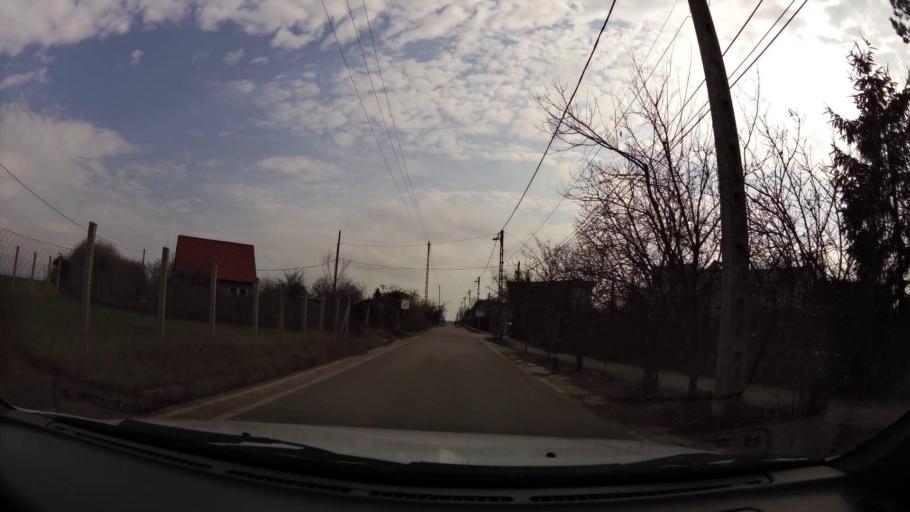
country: HU
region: Pest
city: Csomor
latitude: 47.5252
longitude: 19.2366
